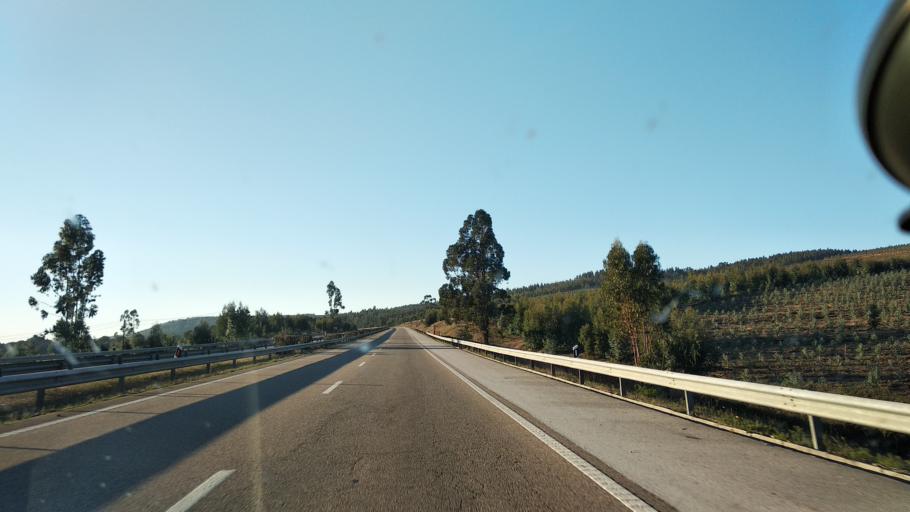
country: PT
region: Santarem
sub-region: Constancia
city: Constancia
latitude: 39.4895
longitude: -8.2914
